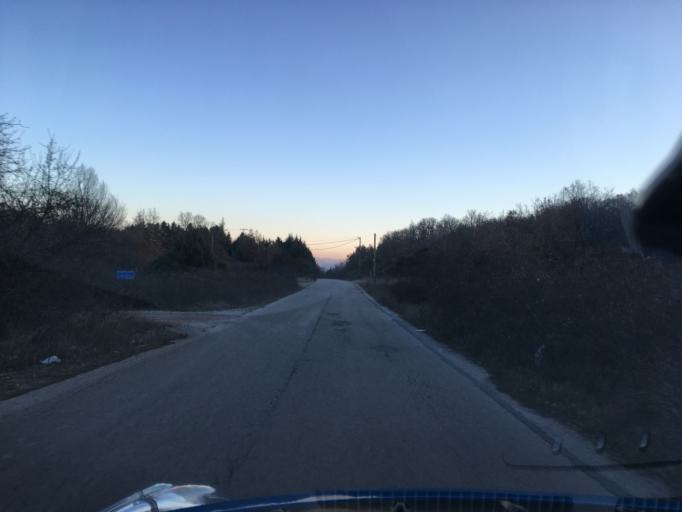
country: GR
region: West Macedonia
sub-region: Nomos Kozanis
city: Kozani
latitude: 40.2629
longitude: 21.7482
